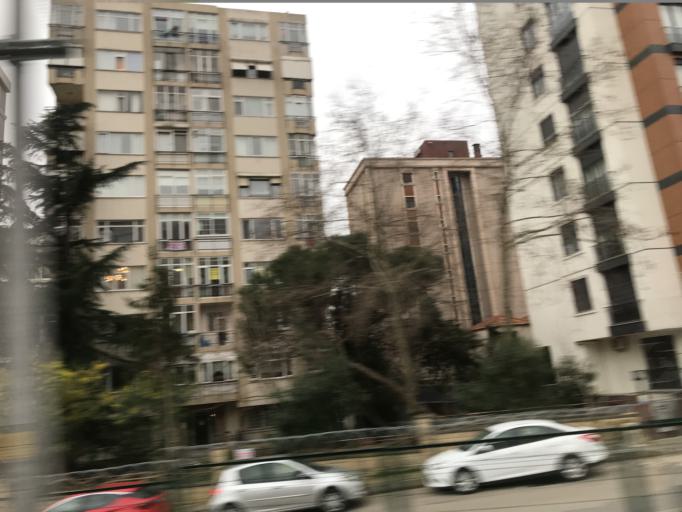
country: TR
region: Istanbul
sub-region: Atasehir
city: Atasehir
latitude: 40.9755
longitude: 29.0721
